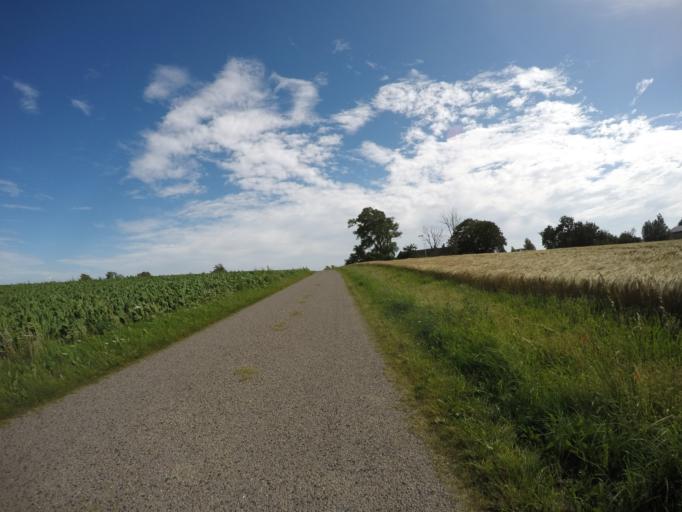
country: SE
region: Skane
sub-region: Tomelilla Kommun
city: Tomelilla
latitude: 55.4721
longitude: 14.1410
